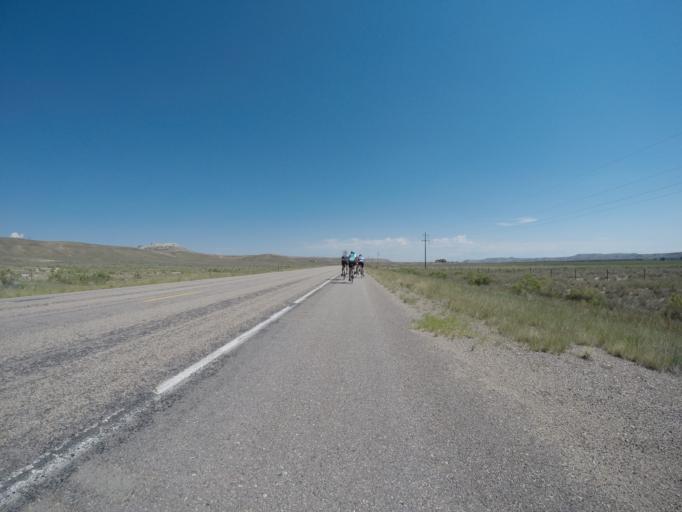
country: US
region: Wyoming
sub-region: Sublette County
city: Marbleton
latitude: 42.3643
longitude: -110.1525
